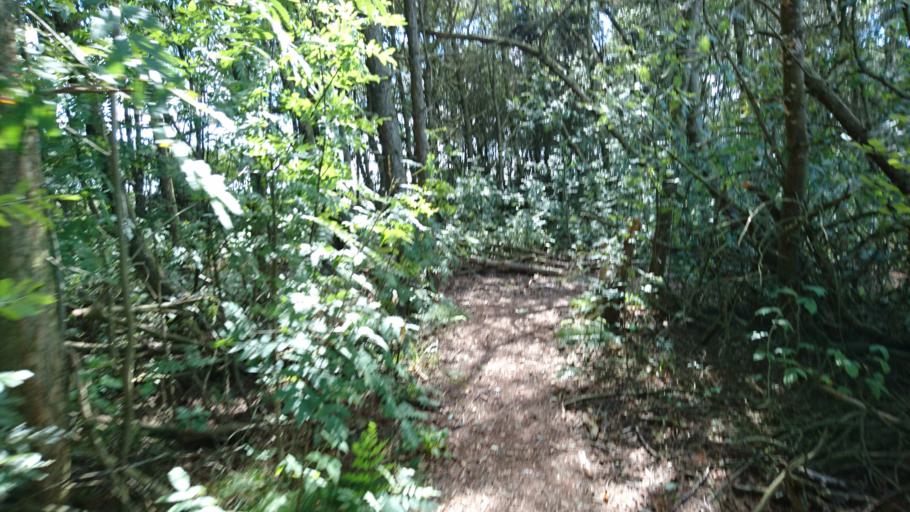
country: DK
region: North Denmark
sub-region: Alborg Kommune
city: Storvorde
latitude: 56.8684
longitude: 10.1786
